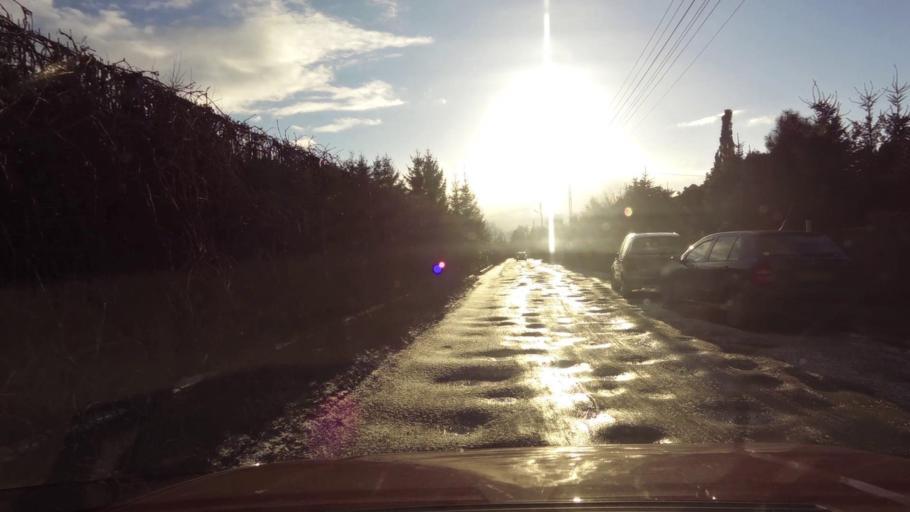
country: PL
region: West Pomeranian Voivodeship
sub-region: Koszalin
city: Koszalin
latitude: 54.1621
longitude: 16.1797
